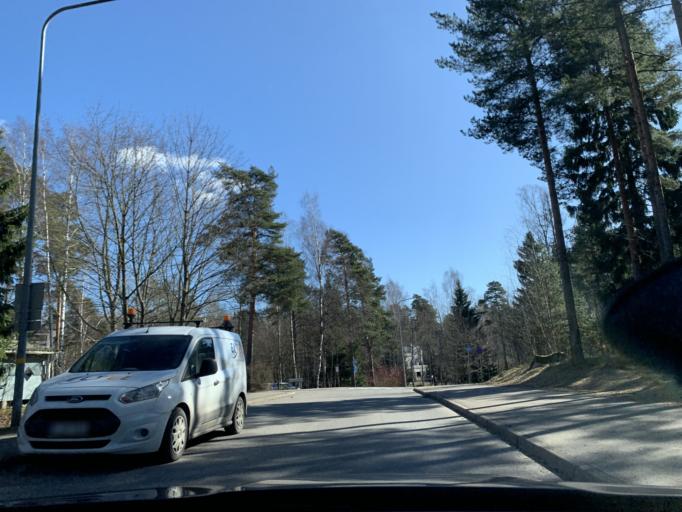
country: FI
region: Uusimaa
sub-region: Helsinki
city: Espoo
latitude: 60.1381
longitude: 24.6615
